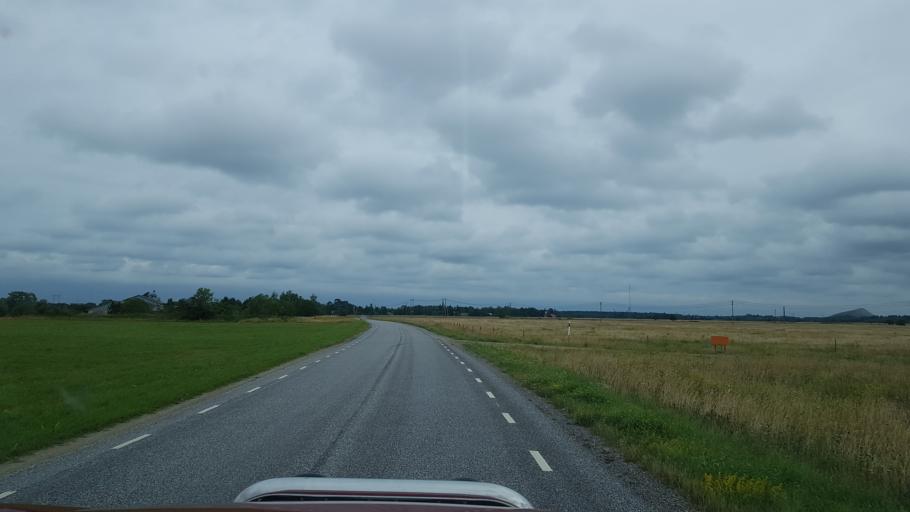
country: EE
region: Ida-Virumaa
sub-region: Puessi linn
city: Pussi
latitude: 59.3918
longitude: 27.0217
